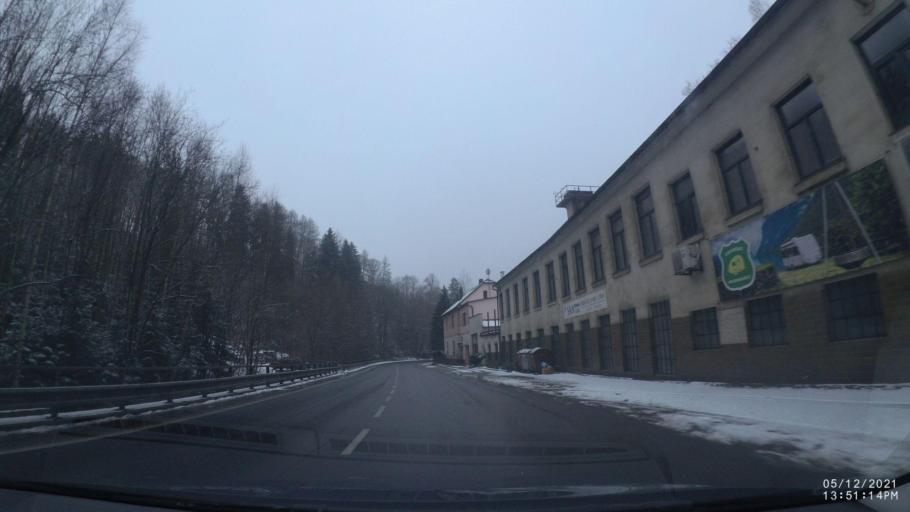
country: CZ
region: Kralovehradecky
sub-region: Okres Nachod
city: Police nad Metuji
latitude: 50.5295
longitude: 16.2249
